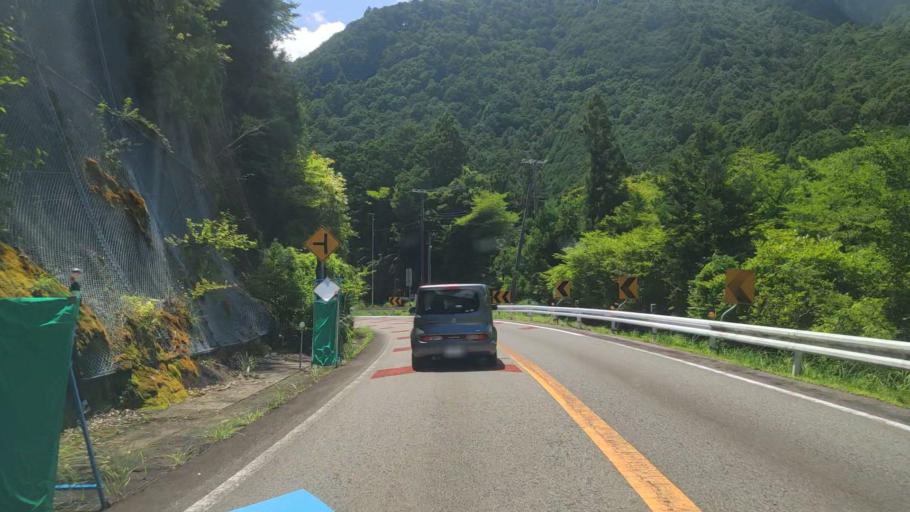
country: JP
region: Mie
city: Owase
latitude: 33.9869
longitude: 136.1087
